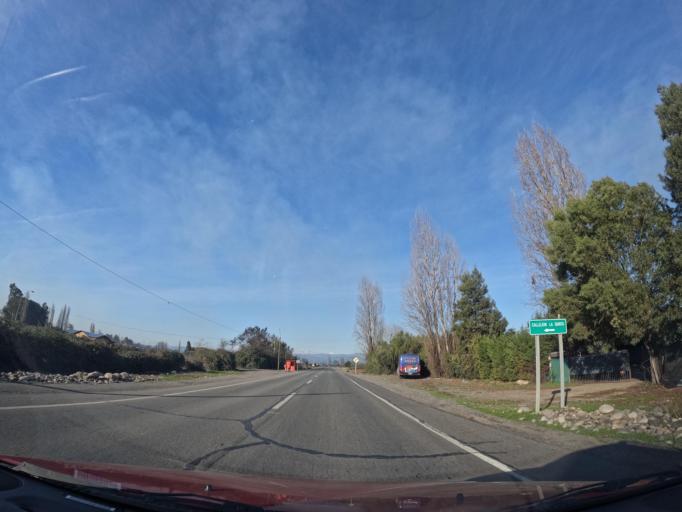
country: CL
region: Maule
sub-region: Provincia de Linares
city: Colbun
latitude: -35.6280
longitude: -71.4537
